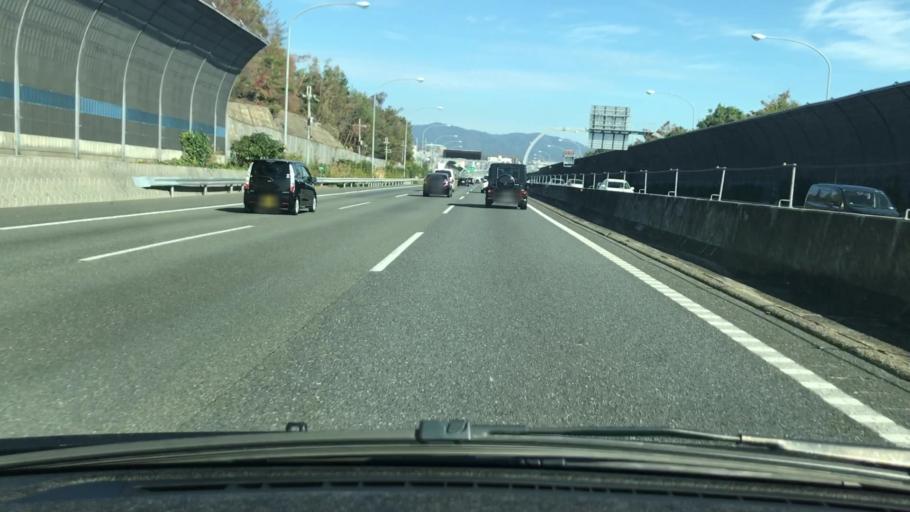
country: JP
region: Osaka
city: Ibaraki
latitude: 34.8245
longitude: 135.5551
